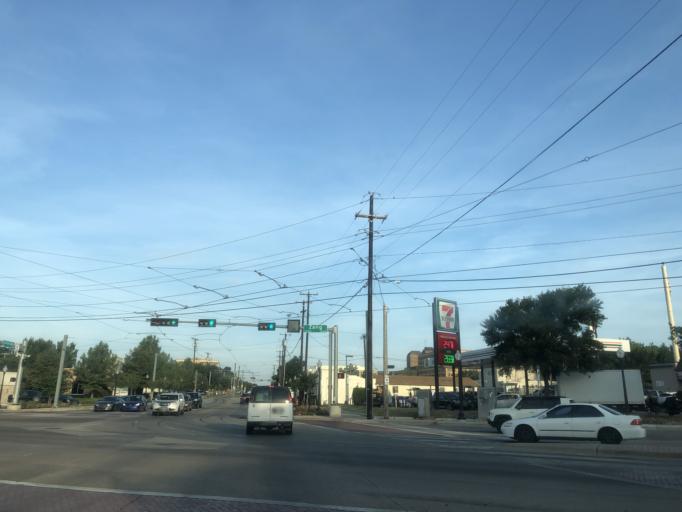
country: US
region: Texas
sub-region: Dallas County
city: Dallas
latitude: 32.7586
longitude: -96.8201
